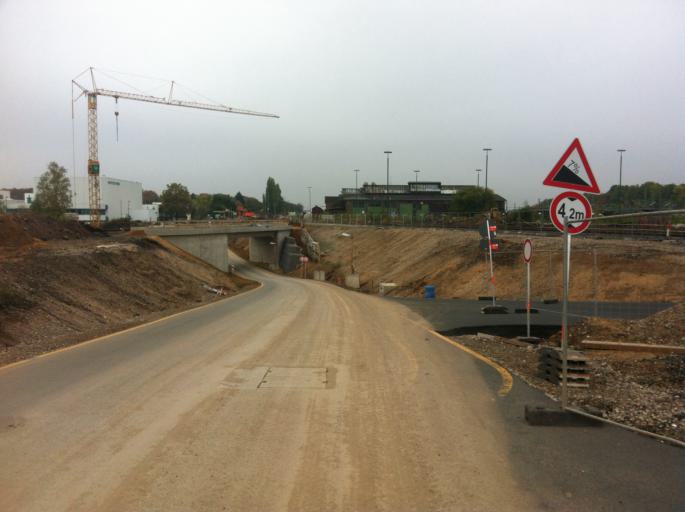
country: DE
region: North Rhine-Westphalia
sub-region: Regierungsbezirk Koln
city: Bilderstoeckchen
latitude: 50.9833
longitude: 6.9203
